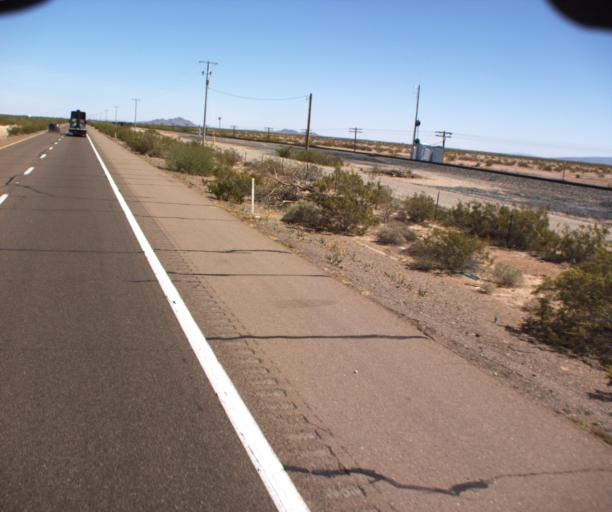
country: US
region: Arizona
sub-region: Yuma County
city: Wellton
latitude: 32.7598
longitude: -113.6371
